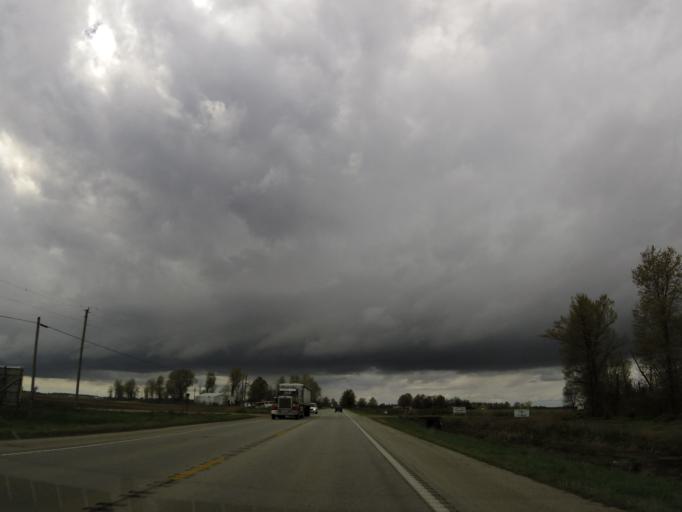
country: US
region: Arkansas
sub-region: Clay County
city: Corning
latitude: 36.5330
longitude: -90.5340
